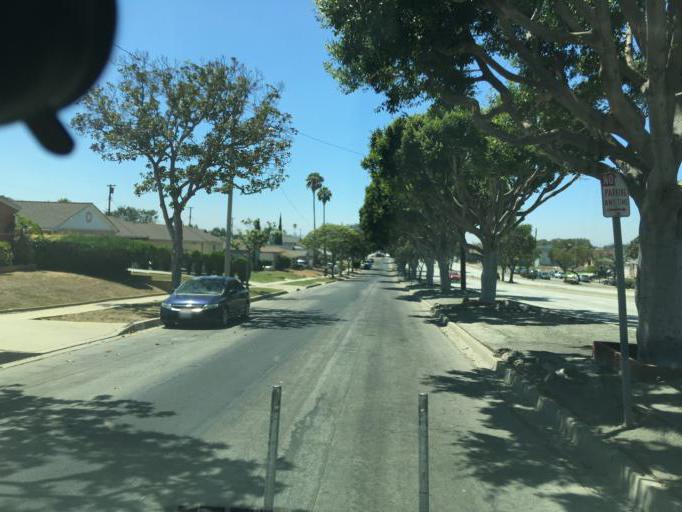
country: US
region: California
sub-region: Los Angeles County
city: West Athens
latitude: 33.9308
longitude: -118.3147
